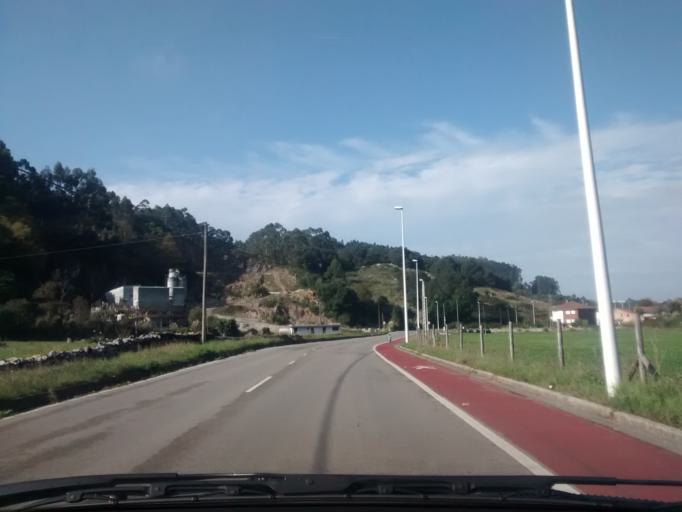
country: ES
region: Cantabria
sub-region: Provincia de Cantabria
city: Entrambasaguas
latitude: 43.3845
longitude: -3.6932
